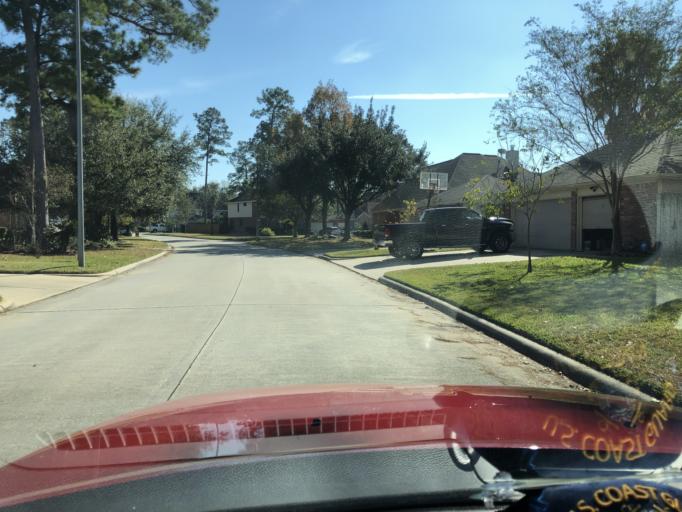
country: US
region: Texas
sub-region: Harris County
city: Tomball
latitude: 30.0203
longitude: -95.5554
